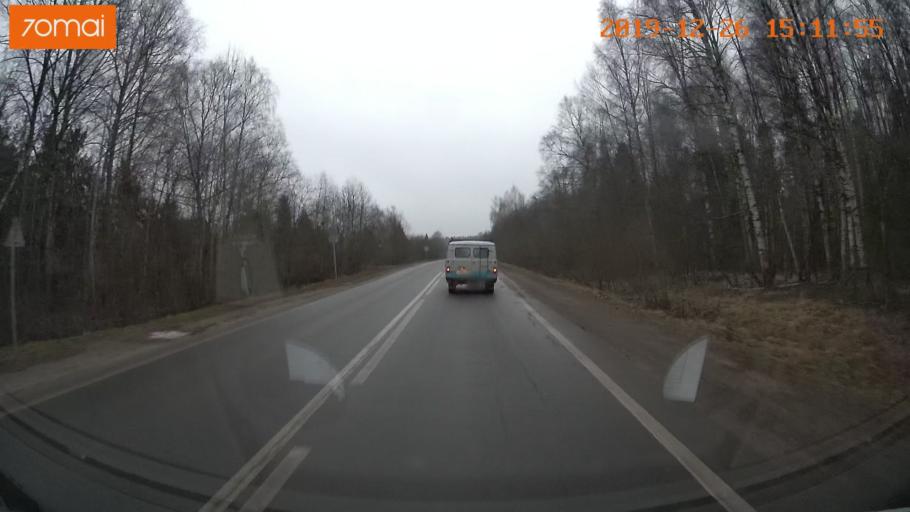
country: RU
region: Jaroslavl
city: Rybinsk
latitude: 58.1319
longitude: 38.8685
